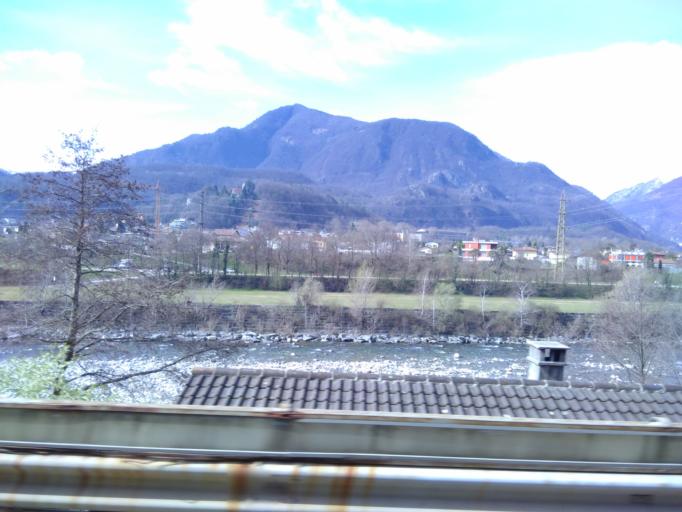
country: CH
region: Ticino
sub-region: Locarno District
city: Losone
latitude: 46.1764
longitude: 8.7641
